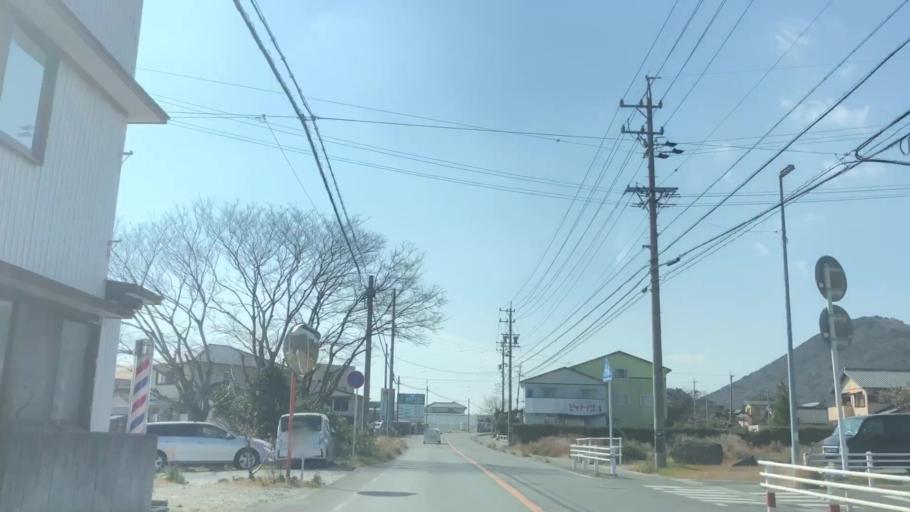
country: JP
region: Aichi
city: Tahara
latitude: 34.6599
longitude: 137.2519
